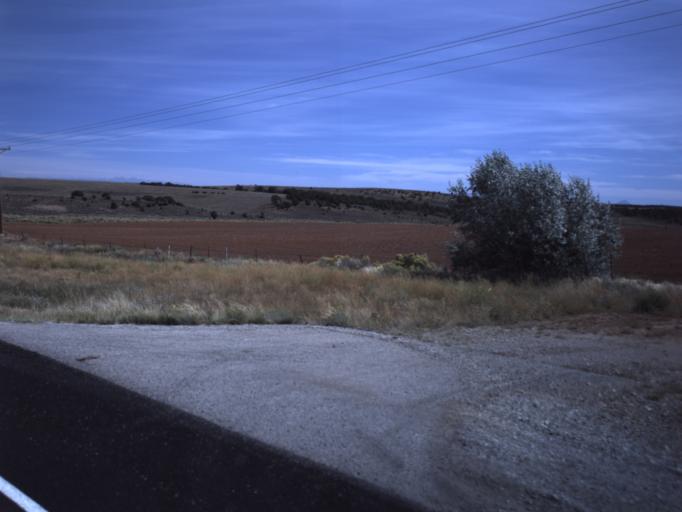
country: US
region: Utah
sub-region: San Juan County
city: Monticello
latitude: 37.8728
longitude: -109.3052
